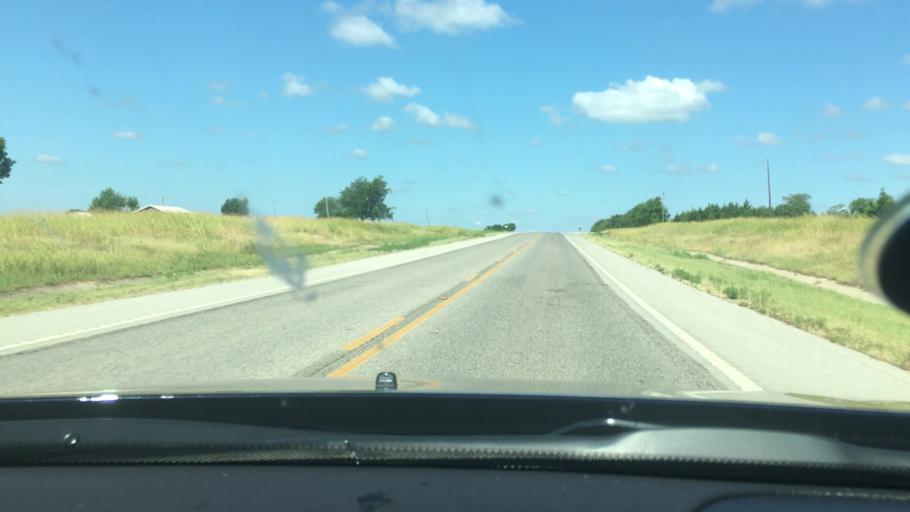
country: US
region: Oklahoma
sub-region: Marshall County
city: Oakland
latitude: 34.1001
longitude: -96.8961
